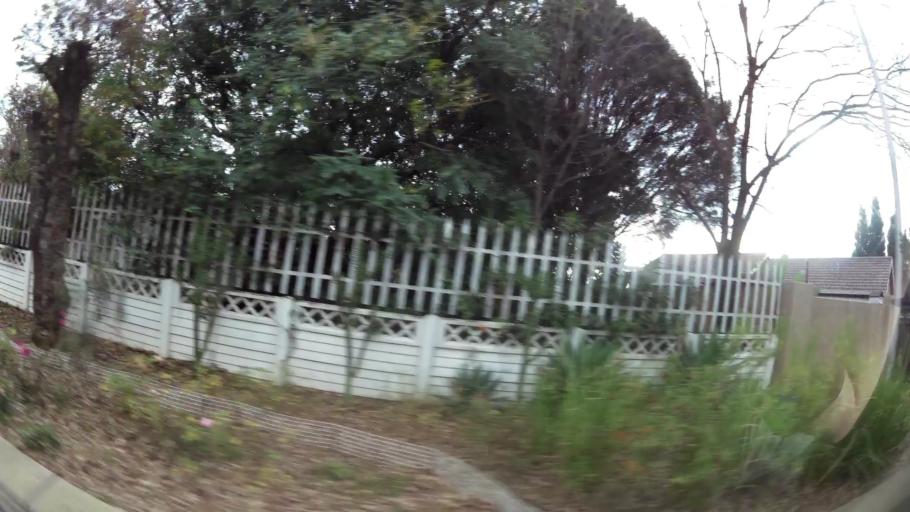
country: ZA
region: Gauteng
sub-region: Ekurhuleni Metropolitan Municipality
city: Benoni
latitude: -26.1246
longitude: 28.3623
